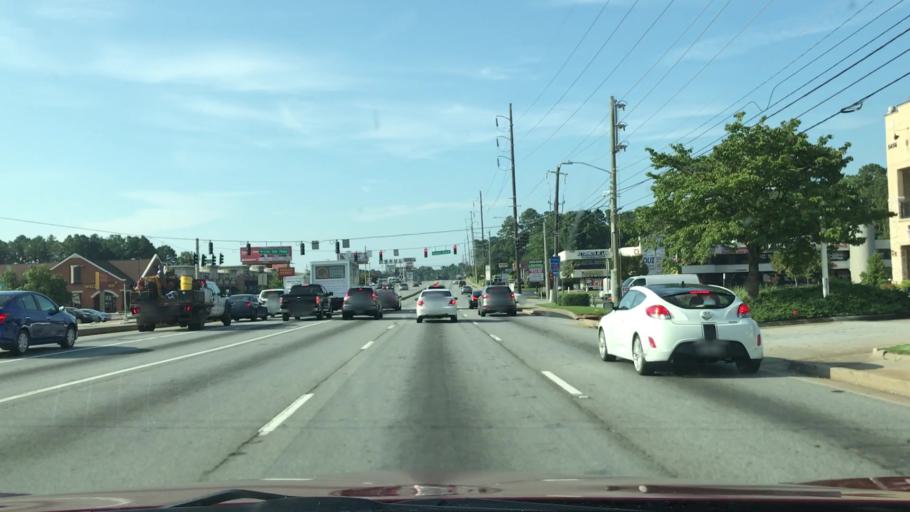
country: US
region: Georgia
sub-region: Gwinnett County
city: Norcross
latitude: 33.9081
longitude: -84.2064
